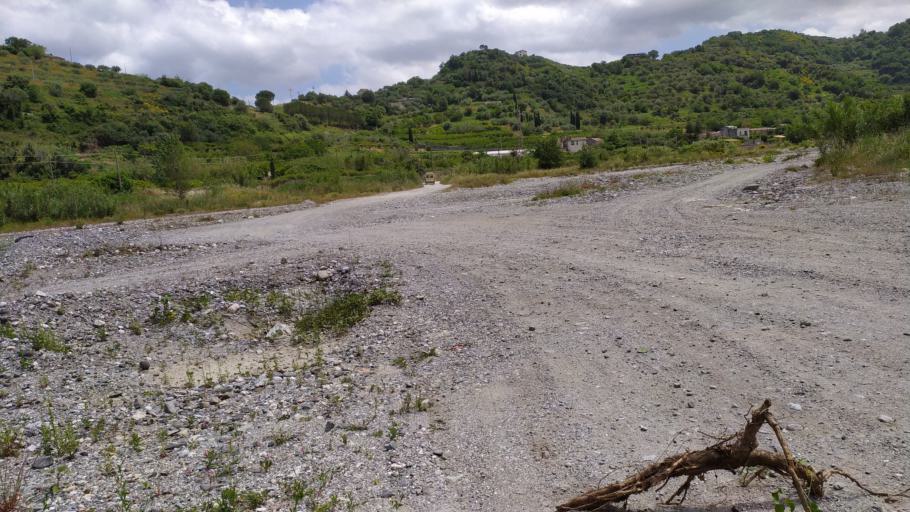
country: IT
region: Sicily
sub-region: Messina
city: San Pier Niceto
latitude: 38.1678
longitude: 15.3605
